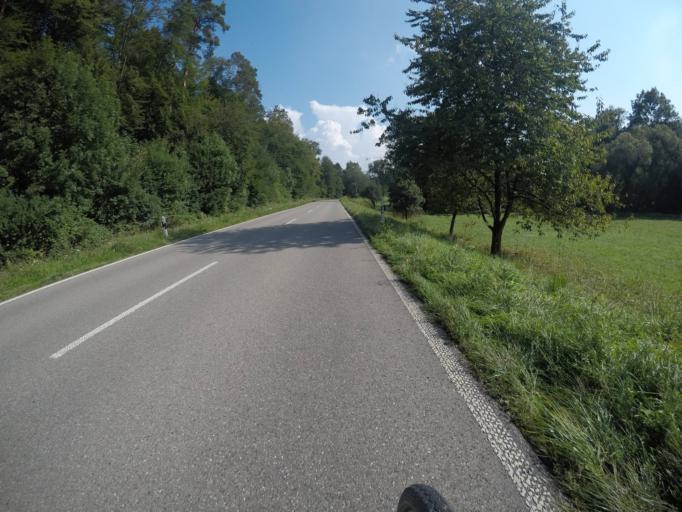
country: DE
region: Baden-Wuerttemberg
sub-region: Regierungsbezirk Stuttgart
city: Filderstadt
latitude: 48.6328
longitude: 9.1913
